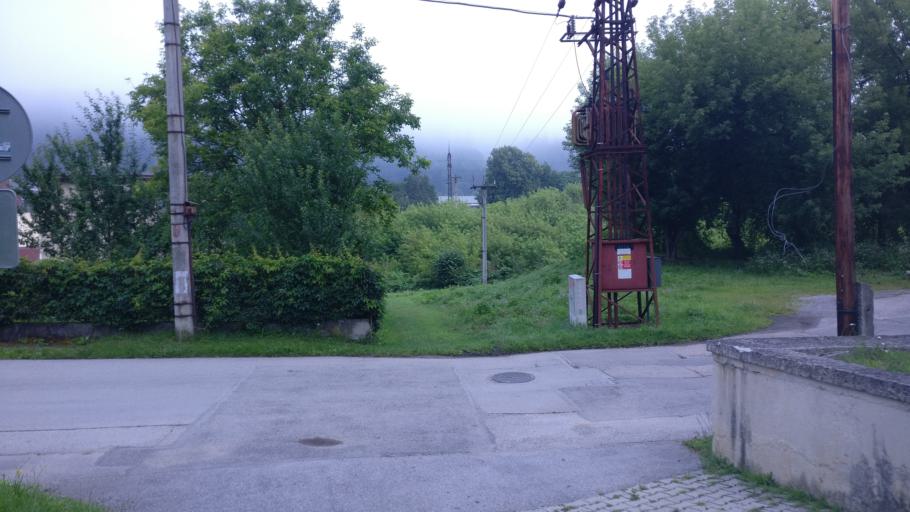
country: SK
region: Zilinsky
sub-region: Okres Zilina
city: Zilina
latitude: 49.2422
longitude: 18.7435
